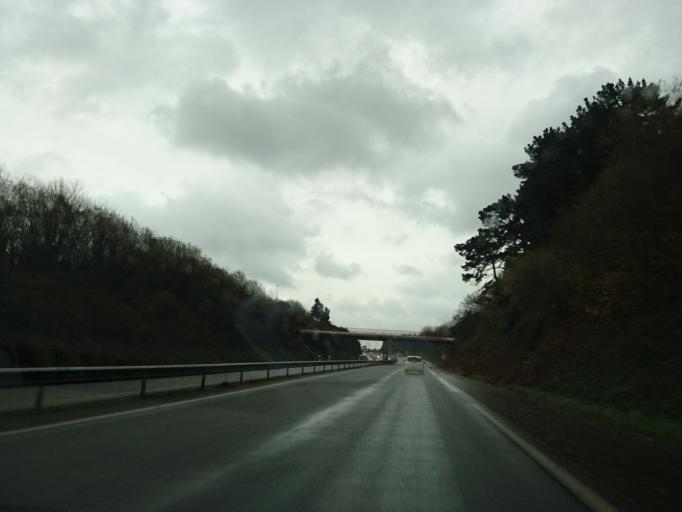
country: FR
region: Brittany
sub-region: Departement du Finistere
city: Guilers
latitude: 48.3823
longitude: -4.5477
